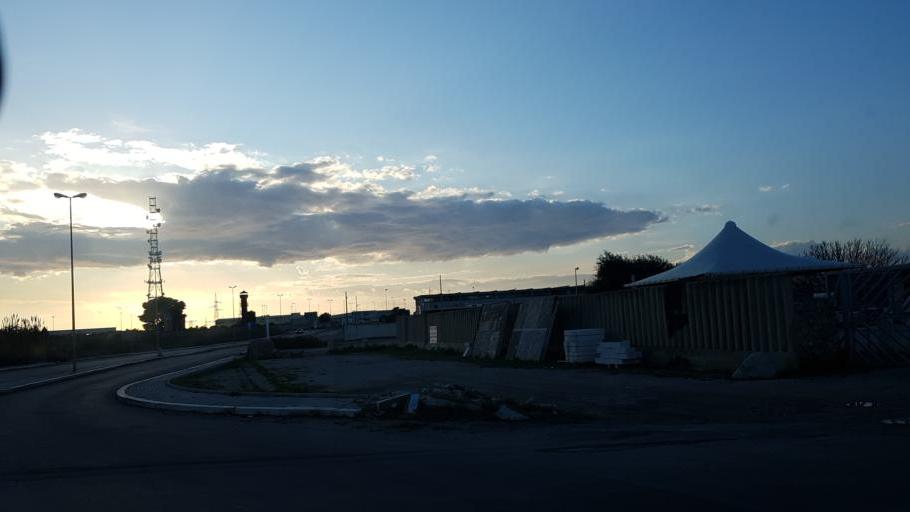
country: IT
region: Apulia
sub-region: Provincia di Lecce
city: Surbo
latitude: 40.3881
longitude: 18.1191
